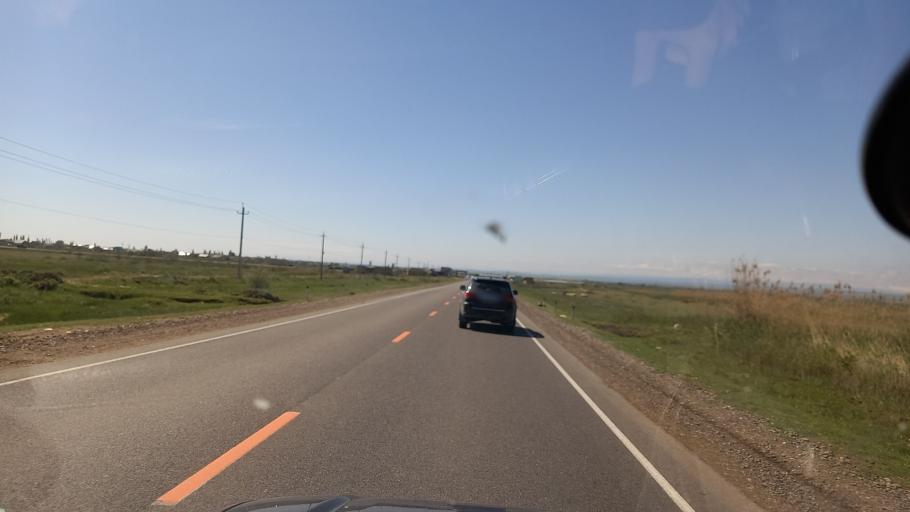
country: RU
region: Dagestan
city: Khazar
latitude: 41.9440
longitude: 48.3261
